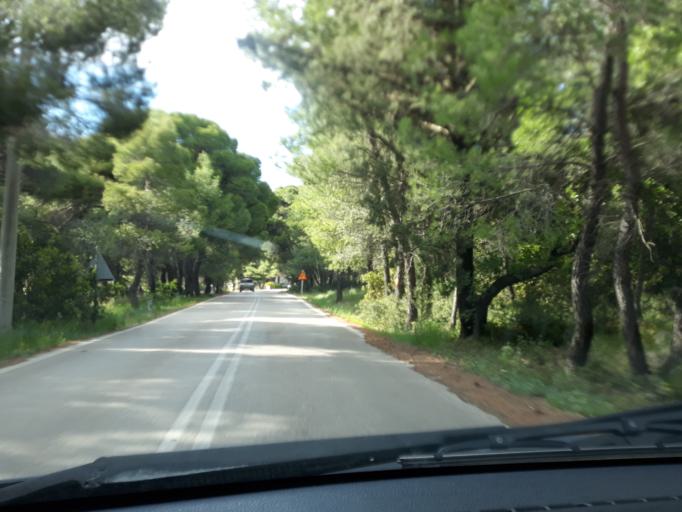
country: GR
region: Attica
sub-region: Nomarchia Anatolikis Attikis
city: Varybobi
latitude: 38.1350
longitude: 23.7917
